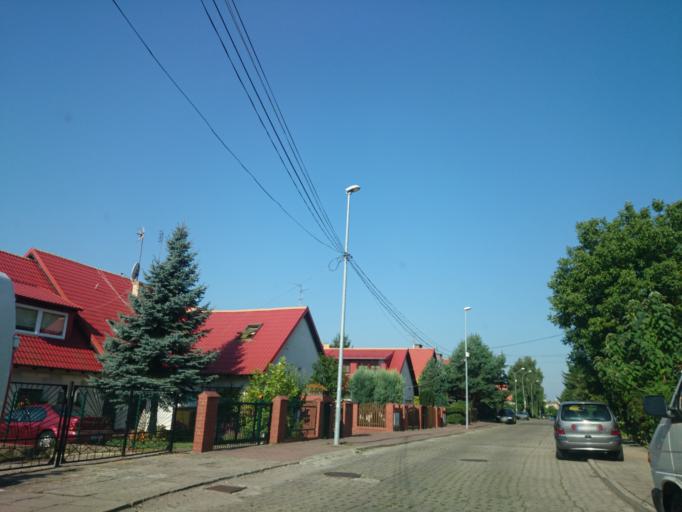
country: PL
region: West Pomeranian Voivodeship
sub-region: Powiat policki
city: Przeclaw
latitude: 53.4170
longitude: 14.4906
